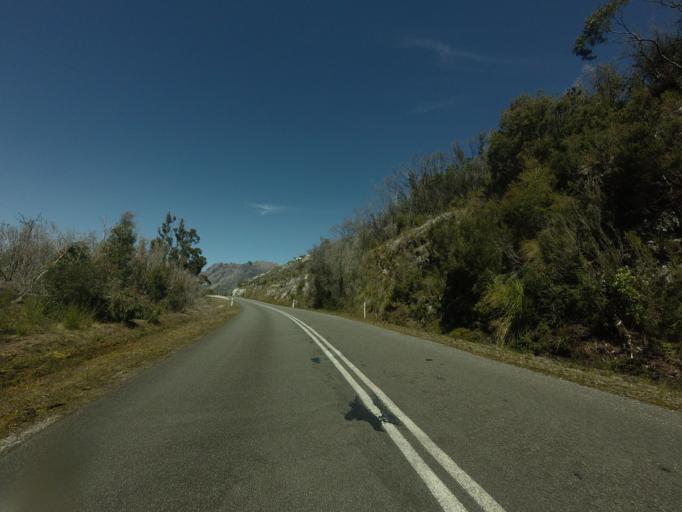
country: AU
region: Tasmania
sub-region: Huon Valley
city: Geeveston
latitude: -42.8512
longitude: 146.1821
